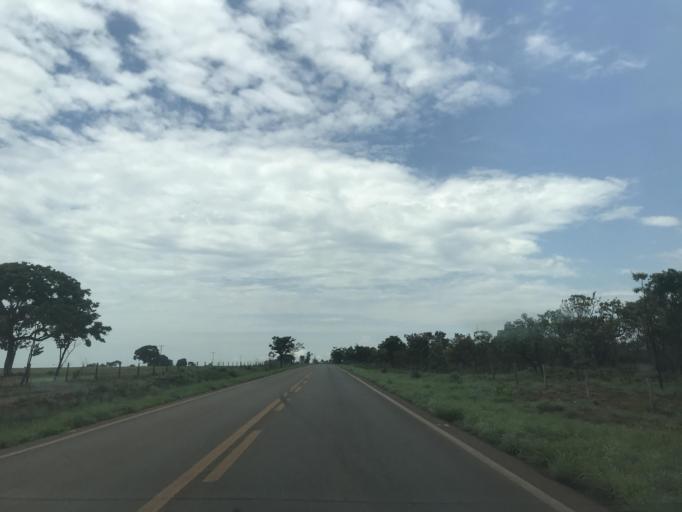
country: BR
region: Goias
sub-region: Luziania
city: Luziania
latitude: -16.2880
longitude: -48.0031
